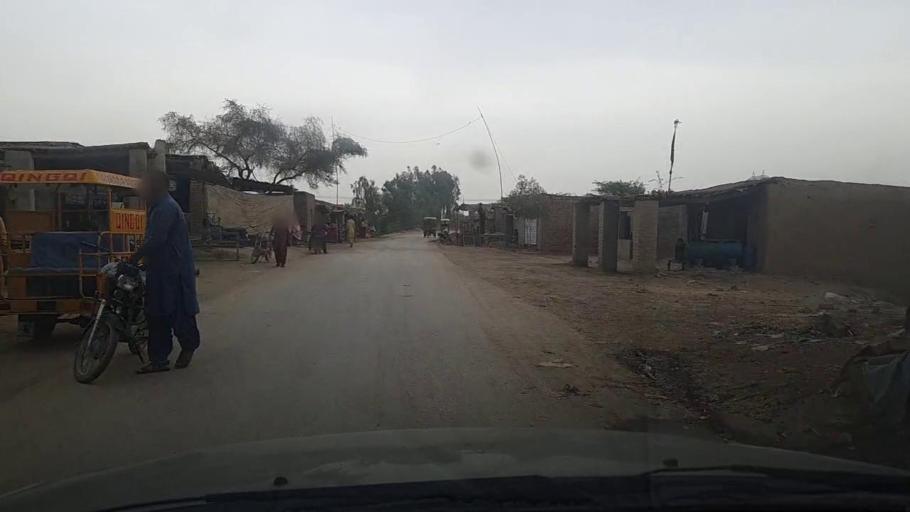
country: PK
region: Sindh
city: Daulatpur
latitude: 26.3423
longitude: 68.1249
